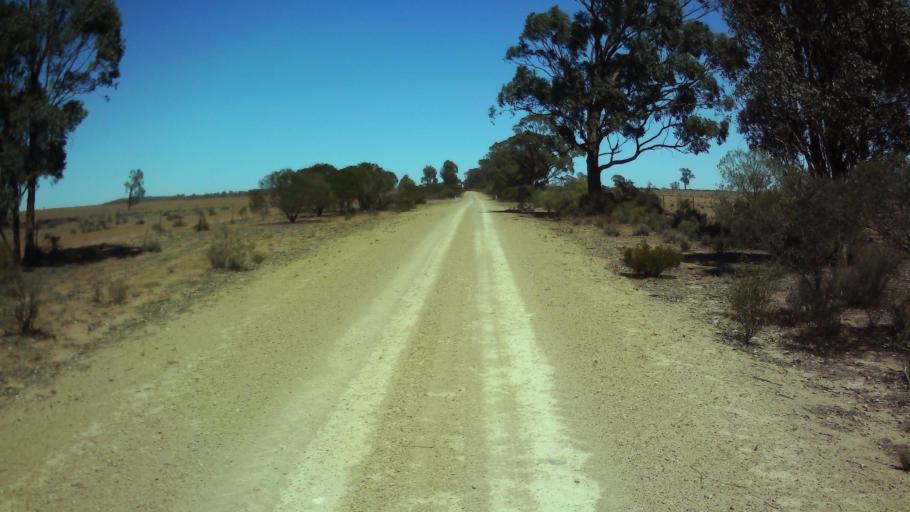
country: AU
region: New South Wales
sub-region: Forbes
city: Forbes
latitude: -33.6941
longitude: 147.8246
